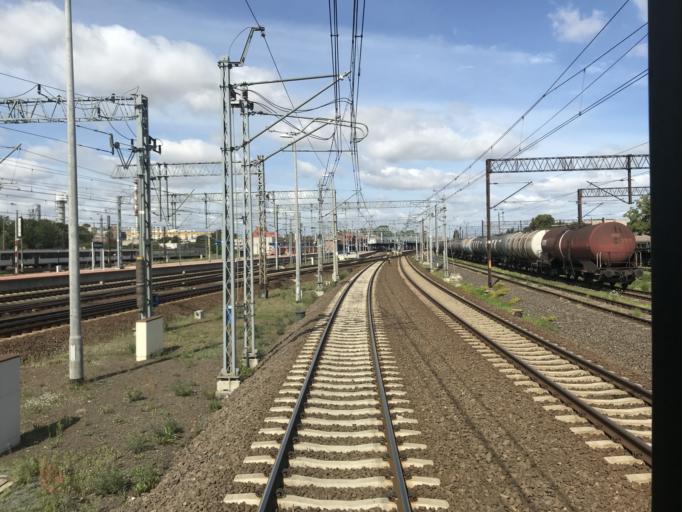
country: PL
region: Pomeranian Voivodeship
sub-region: Powiat malborski
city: Malbork
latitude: 54.0348
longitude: 19.0479
